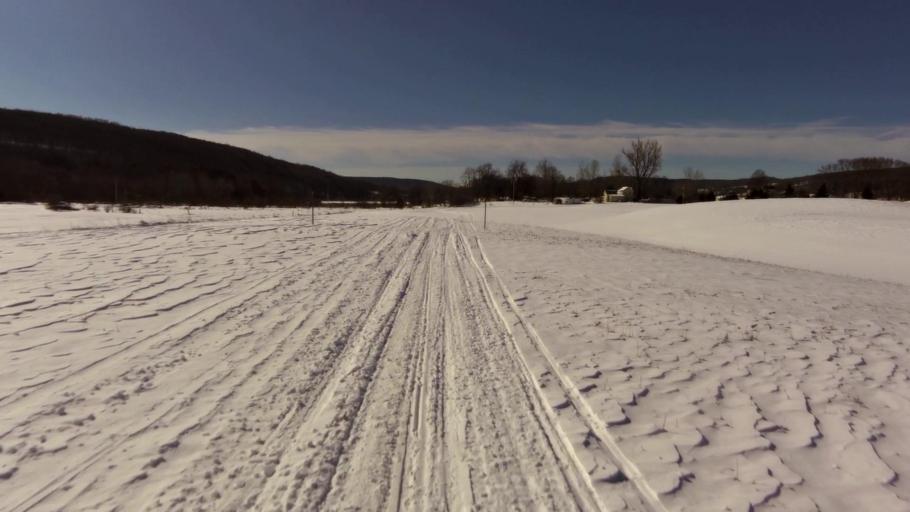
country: US
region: New York
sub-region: Allegany County
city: Cuba
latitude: 42.3333
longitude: -78.3060
